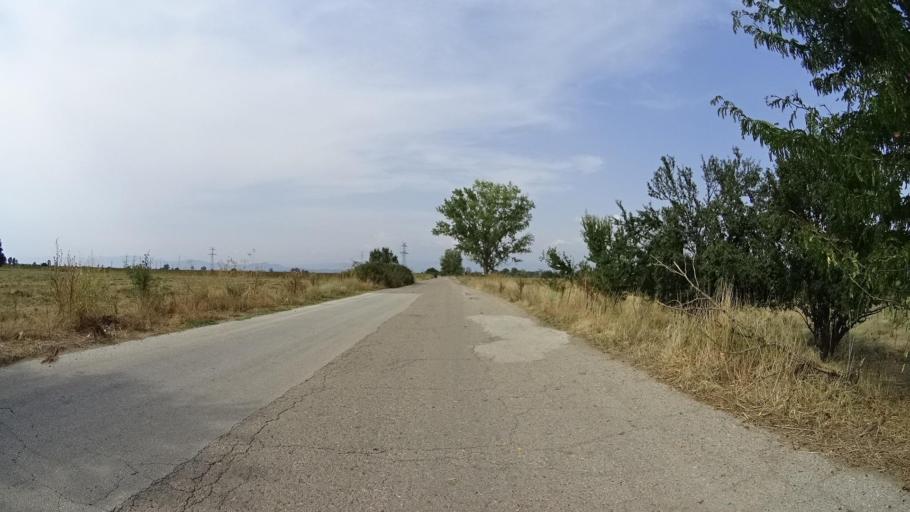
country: BG
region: Plovdiv
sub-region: Obshtina Kaloyanovo
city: Kaloyanovo
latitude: 42.3187
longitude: 24.7992
